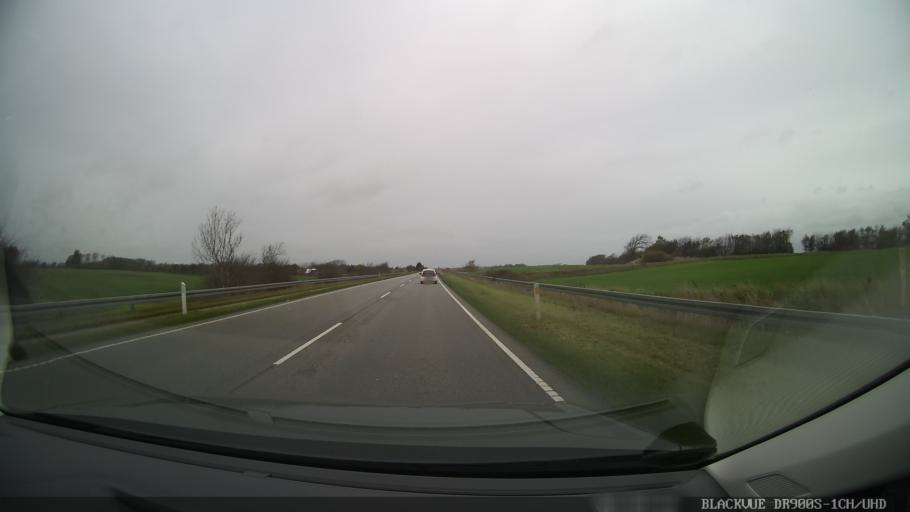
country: DK
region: North Denmark
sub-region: Thisted Kommune
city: Thisted
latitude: 56.8391
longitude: 8.7028
